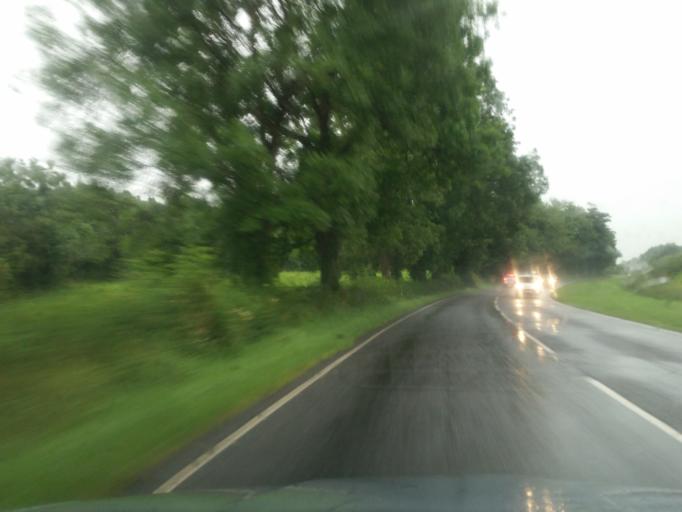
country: GB
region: Northern Ireland
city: Lisnaskea
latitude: 54.2310
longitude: -7.4187
